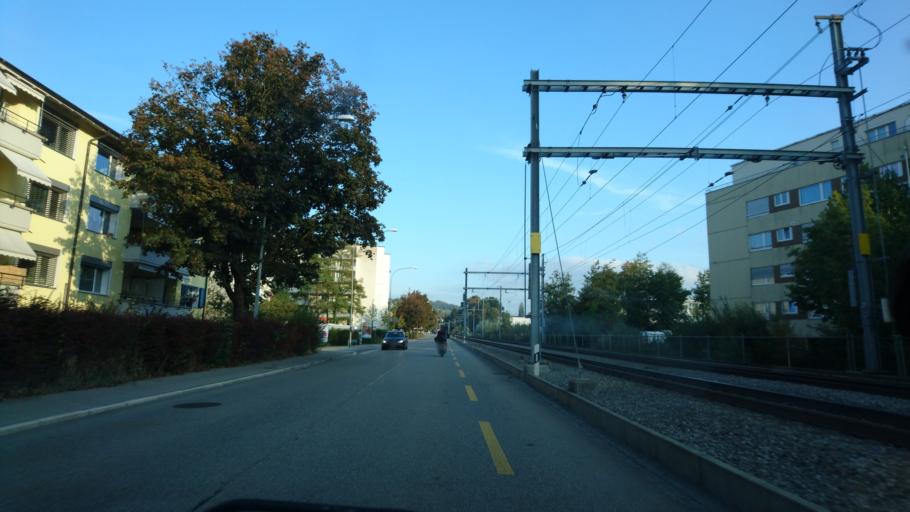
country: CH
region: Bern
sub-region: Bern-Mittelland District
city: Bolligen
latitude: 46.9725
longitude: 7.4875
